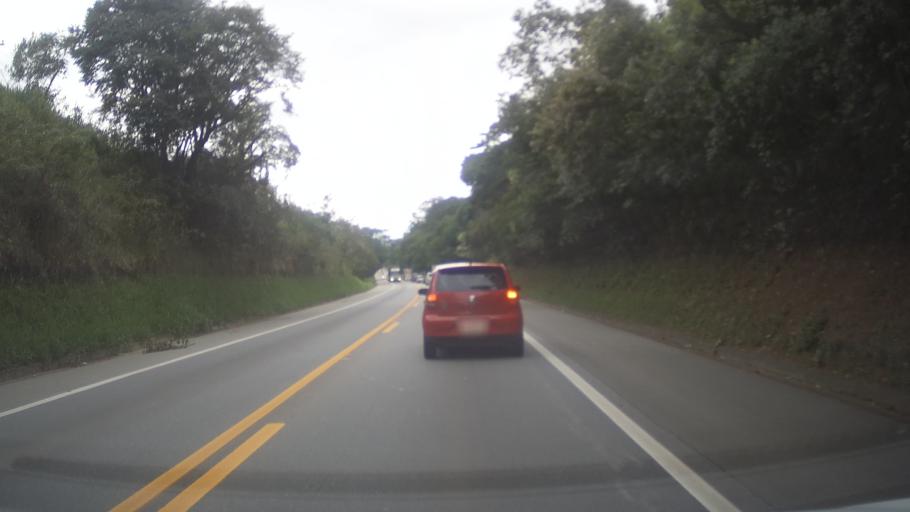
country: BR
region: Sao Paulo
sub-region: Francisco Morato
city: Francisco Morato
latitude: -23.2971
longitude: -46.8080
